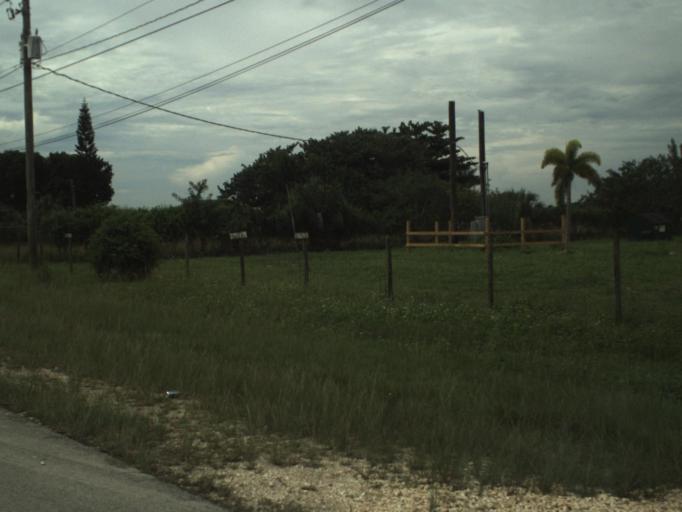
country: US
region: Florida
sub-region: Miami-Dade County
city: Naranja
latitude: 25.5454
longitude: -80.4781
